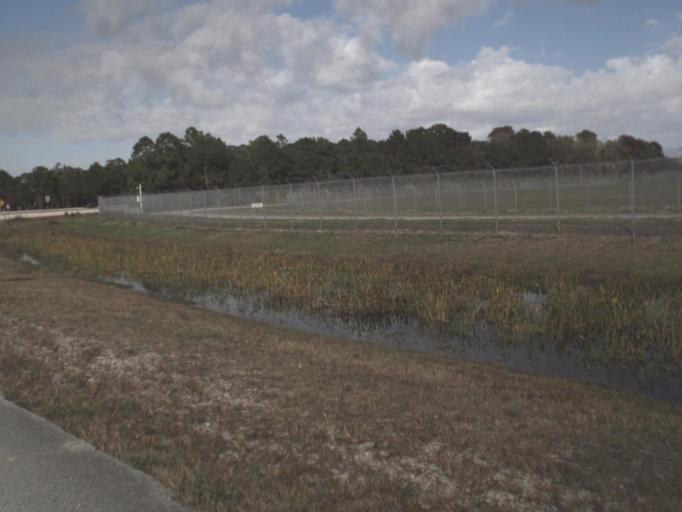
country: US
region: Florida
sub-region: Volusia County
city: Daytona Beach
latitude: 29.1720
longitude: -81.0807
